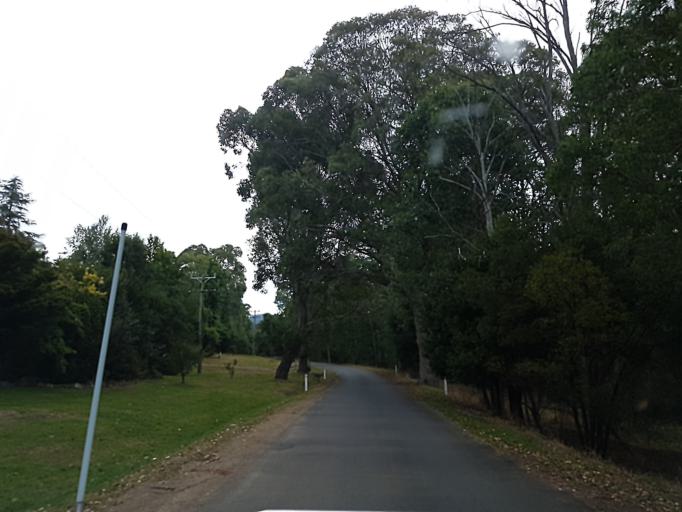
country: AU
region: Victoria
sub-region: Alpine
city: Mount Beauty
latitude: -36.8968
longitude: 147.0609
